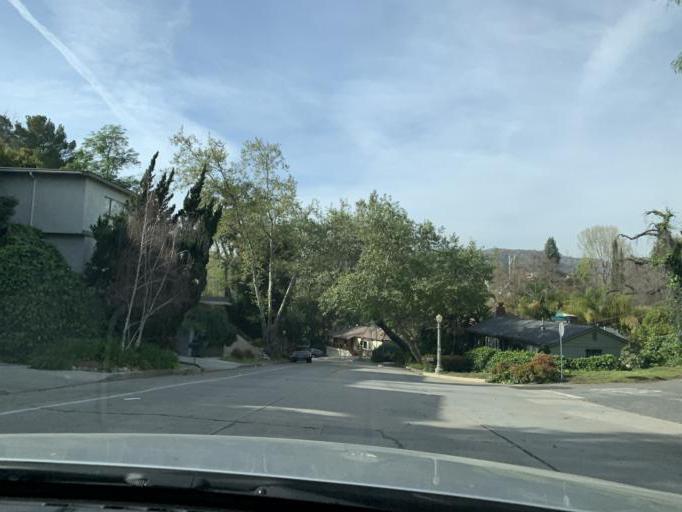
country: US
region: California
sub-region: Los Angeles County
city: South Pasadena
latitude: 34.1355
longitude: -118.1841
